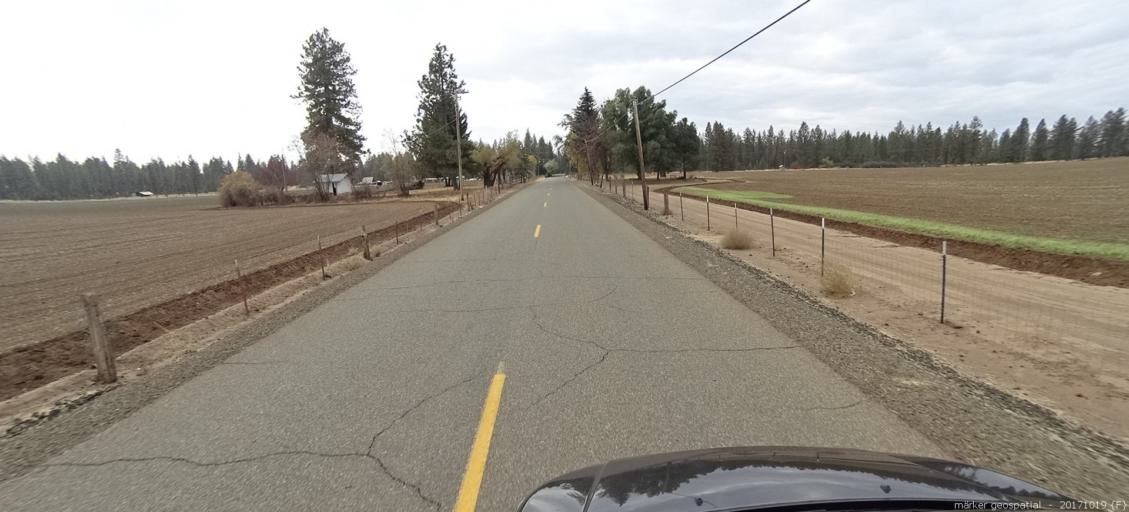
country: US
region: California
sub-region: Shasta County
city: Burney
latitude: 41.0685
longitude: -121.3651
